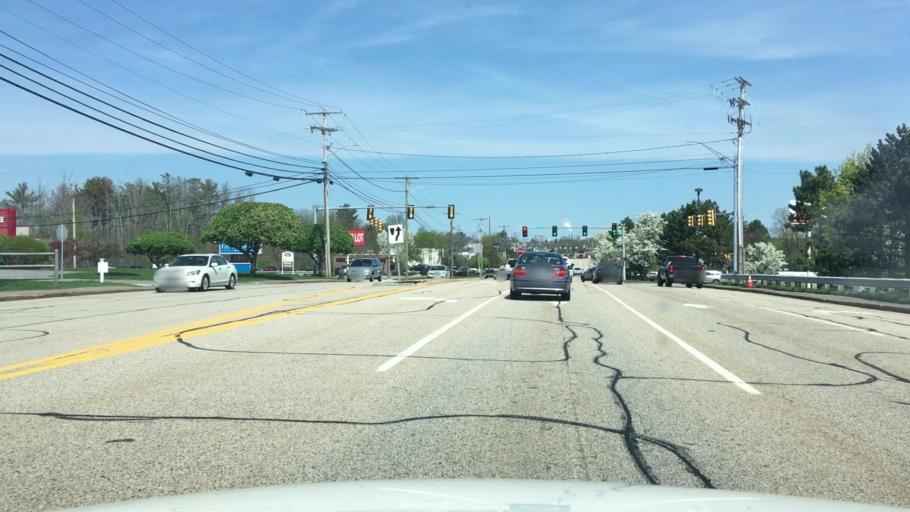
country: US
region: Maine
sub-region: York County
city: South Eliot
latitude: 43.0897
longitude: -70.7912
